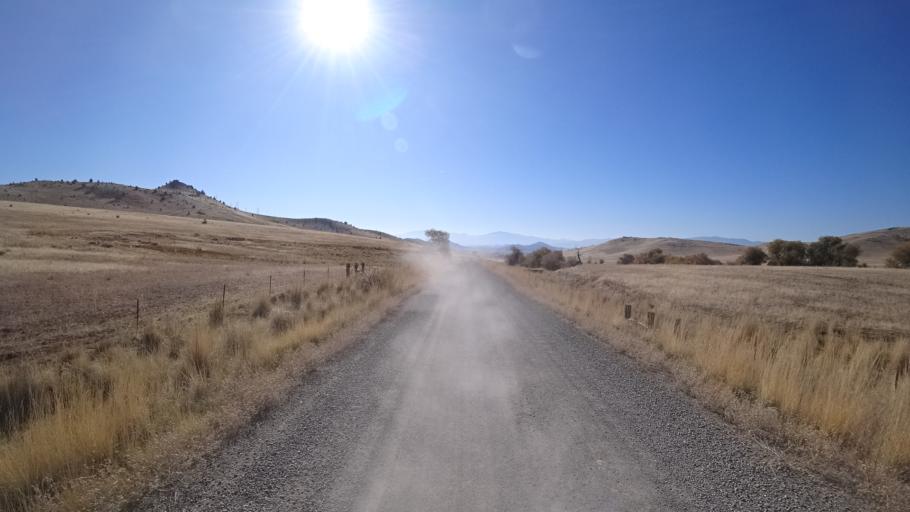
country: US
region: California
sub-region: Siskiyou County
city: Montague
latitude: 41.7483
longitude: -122.3621
